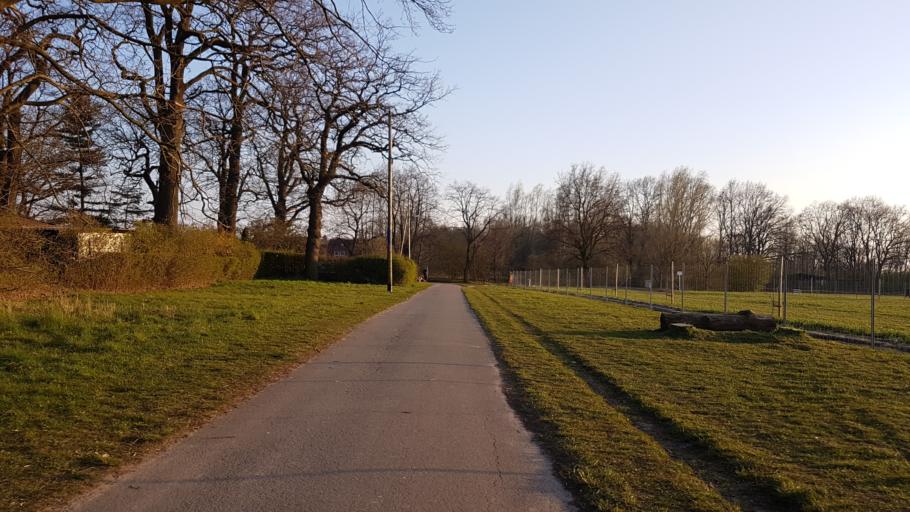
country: DE
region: Lower Saxony
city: Langenhagen
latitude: 52.4271
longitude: 9.6995
